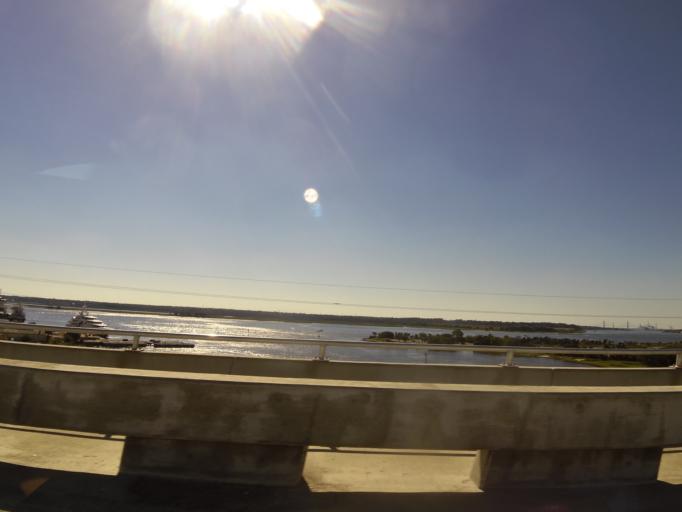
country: US
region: Florida
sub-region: Duval County
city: Atlantic Beach
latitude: 30.3940
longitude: -81.4594
